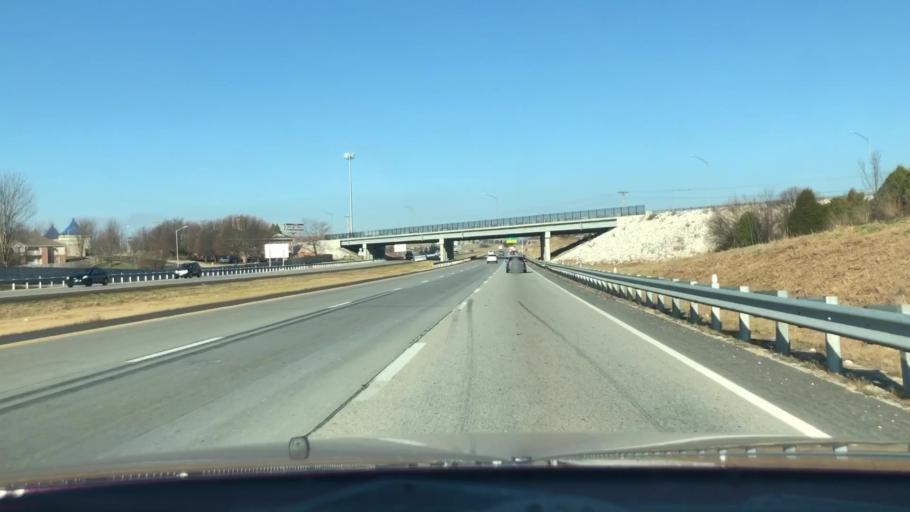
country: US
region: Missouri
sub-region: Greene County
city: Battlefield
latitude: 37.1372
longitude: -93.3087
